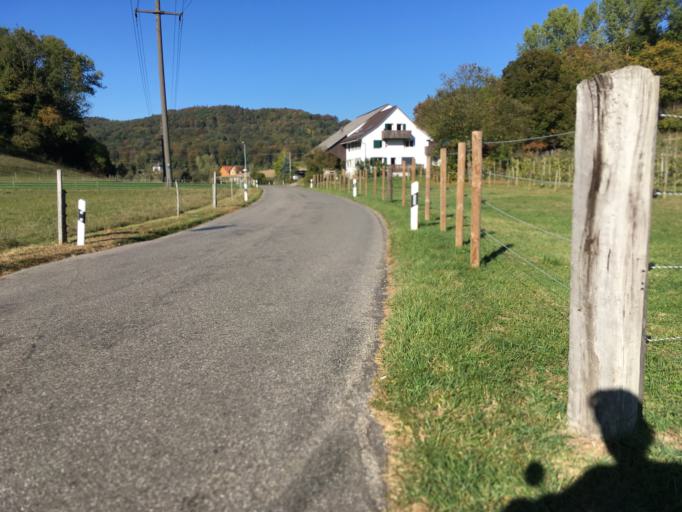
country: CH
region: Zurich
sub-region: Bezirk Buelach
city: Buelach / Soligaenter
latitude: 47.5420
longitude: 8.5422
